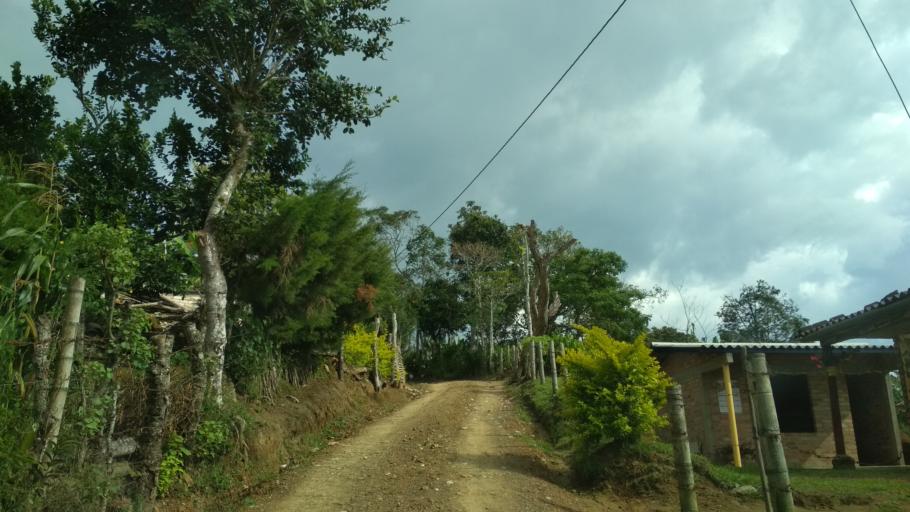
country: CO
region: Cauca
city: Lopez
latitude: 2.4018
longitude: -76.7126
